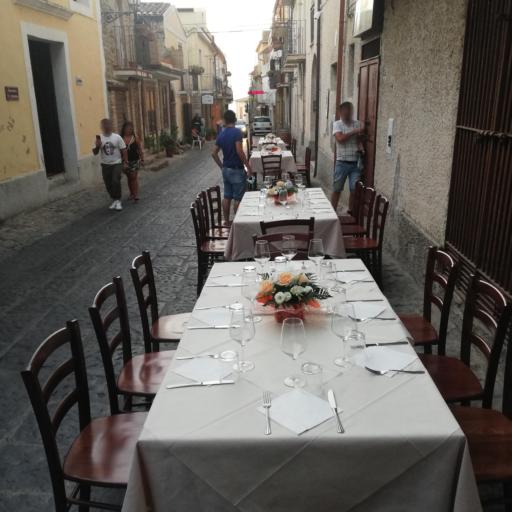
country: IT
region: Calabria
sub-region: Provincia di Cosenza
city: Cariati
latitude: 39.4963
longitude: 16.9467
